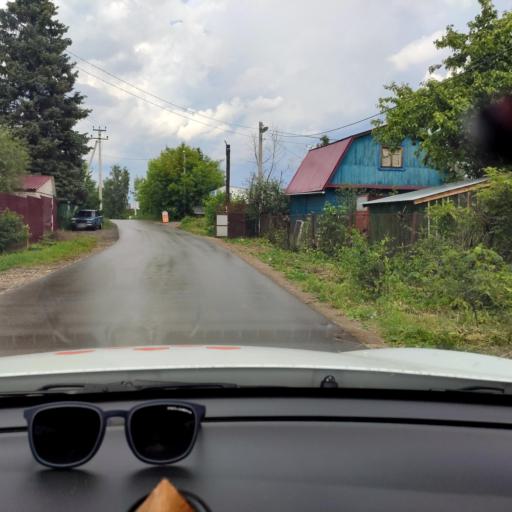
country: RU
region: Tatarstan
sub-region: Zelenodol'skiy Rayon
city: Vasil'yevo
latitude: 55.8265
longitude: 48.7207
